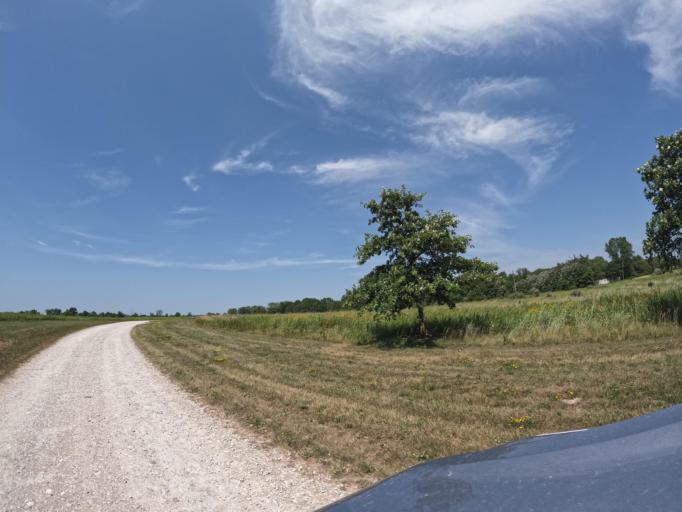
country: US
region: Iowa
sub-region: Henry County
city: Mount Pleasant
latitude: 40.9394
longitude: -91.5832
